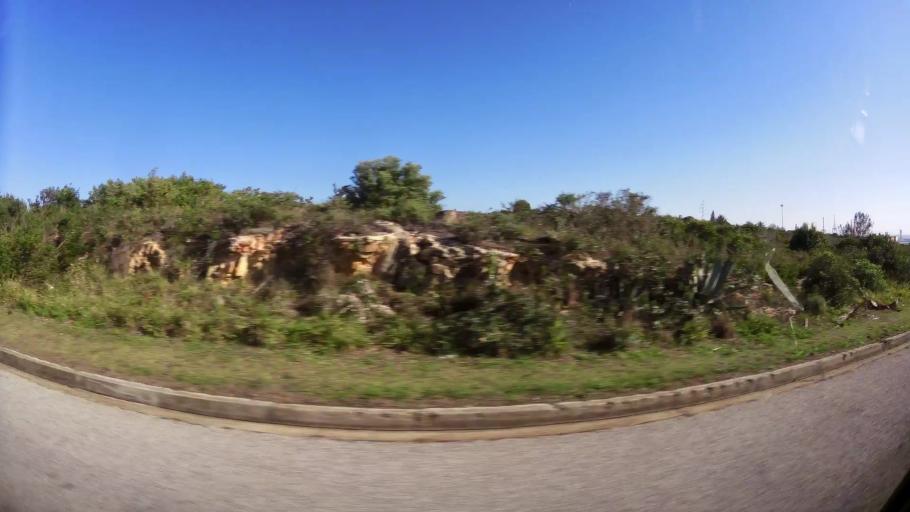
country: ZA
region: Eastern Cape
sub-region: Nelson Mandela Bay Metropolitan Municipality
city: Port Elizabeth
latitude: -33.9759
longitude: 25.6363
